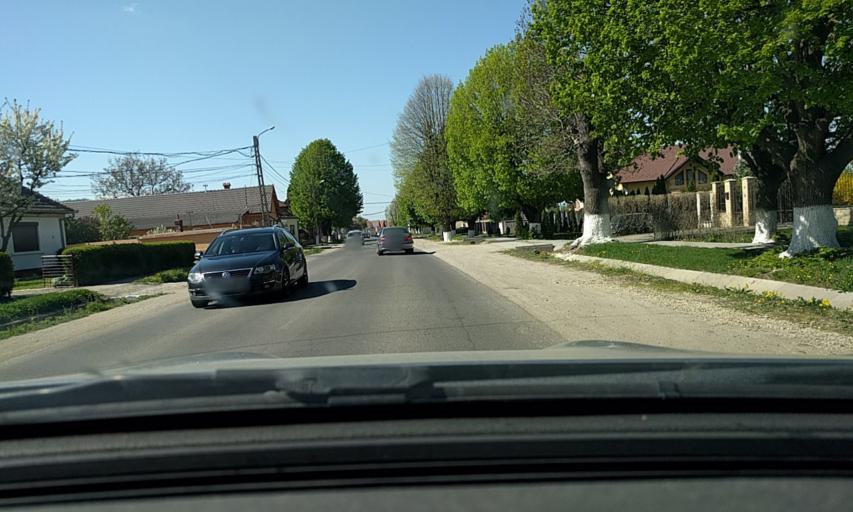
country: RO
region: Brasov
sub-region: Comuna Harman
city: Harman
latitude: 45.7081
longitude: 25.6866
